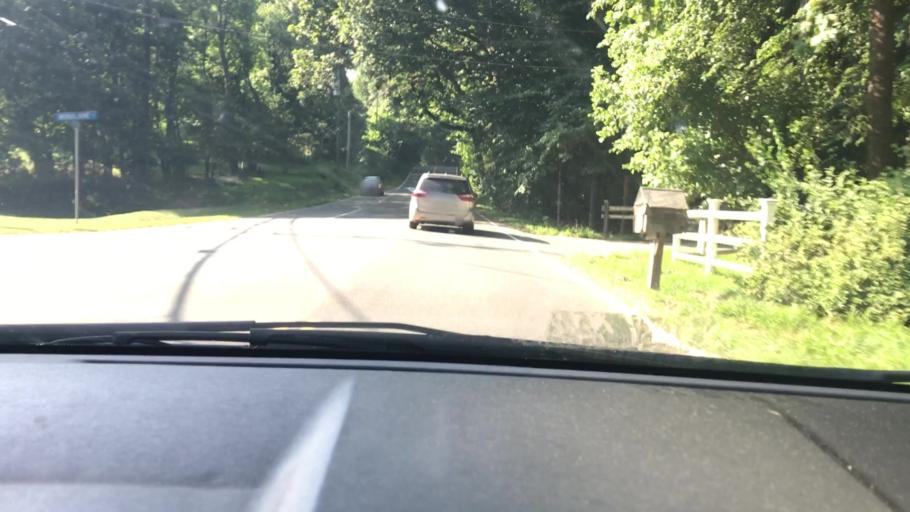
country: US
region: Virginia
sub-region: Fairfax County
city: Great Falls
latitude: 39.0096
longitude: -77.2666
